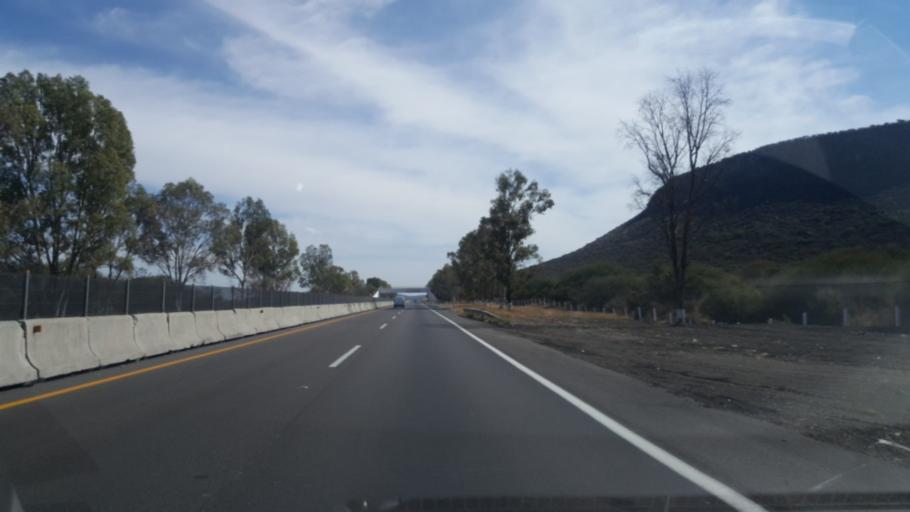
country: MX
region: Jalisco
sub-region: Lagos de Moreno
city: Cristeros [Fraccionamiento]
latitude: 21.2949
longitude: -102.0124
